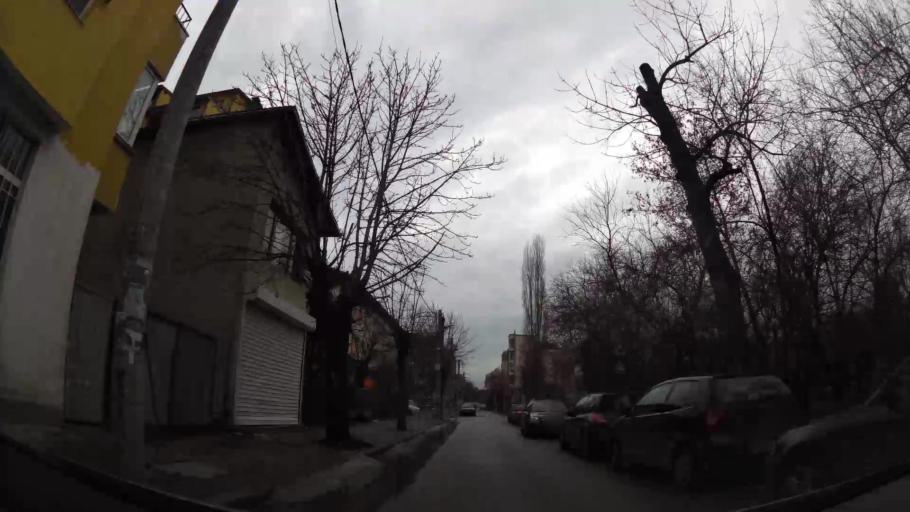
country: BG
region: Sofia-Capital
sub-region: Stolichna Obshtina
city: Sofia
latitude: 42.7221
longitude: 23.3059
